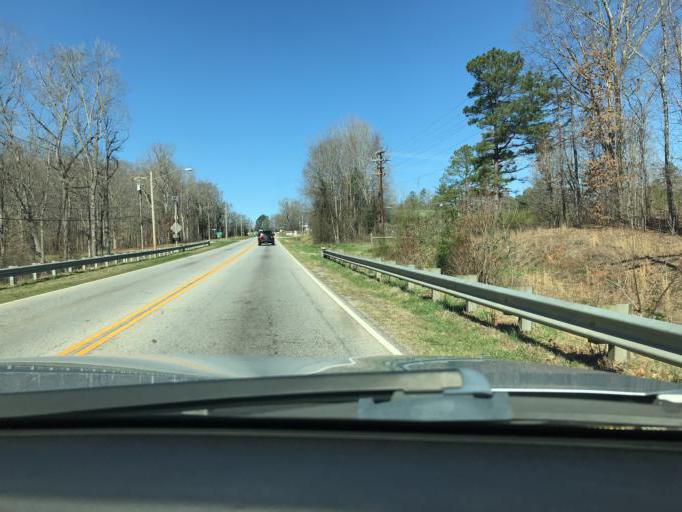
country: US
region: South Carolina
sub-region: Laurens County
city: Watts Mills
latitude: 34.5006
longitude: -81.9898
